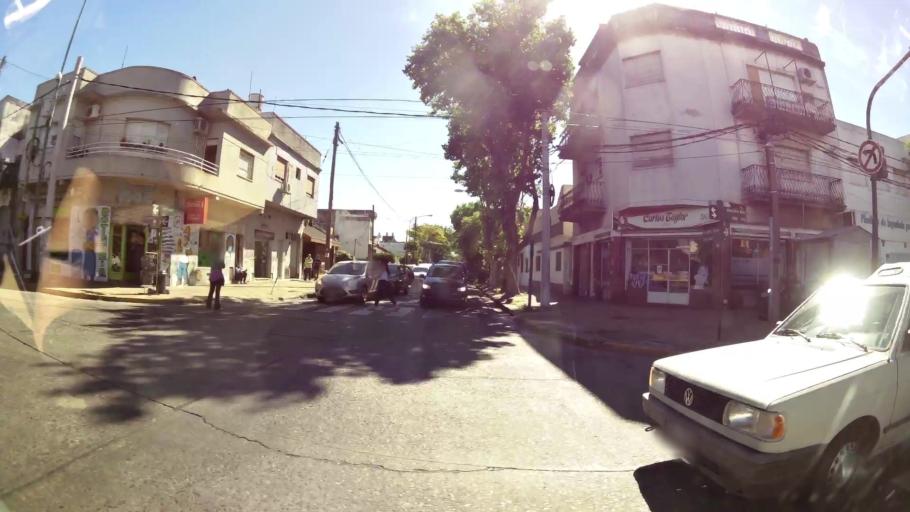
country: AR
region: Buenos Aires
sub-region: Partido de Vicente Lopez
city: Olivos
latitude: -34.5330
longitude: -58.5100
